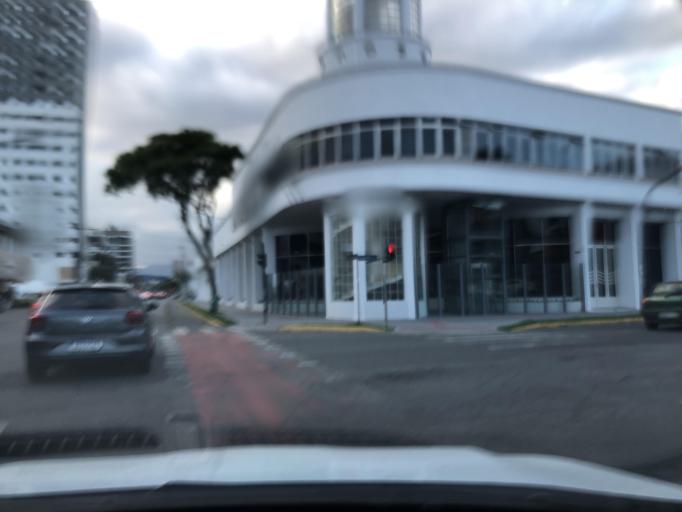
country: BR
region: Santa Catarina
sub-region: Joinville
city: Joinville
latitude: -26.2948
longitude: -48.8478
